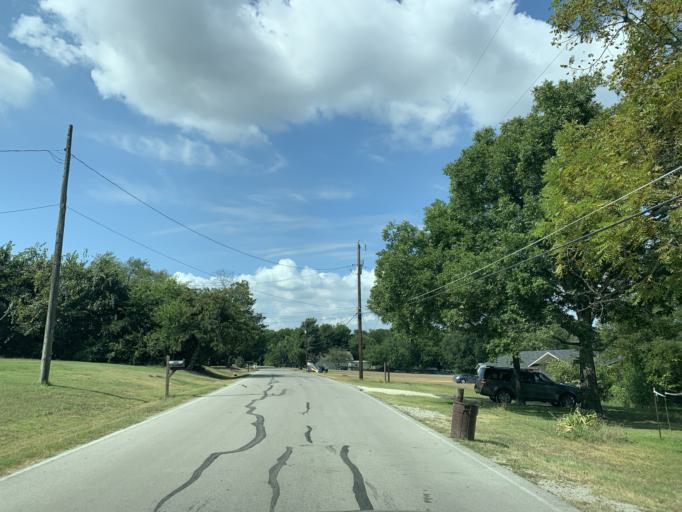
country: US
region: Texas
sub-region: Tarrant County
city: Azle
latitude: 32.8673
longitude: -97.5272
